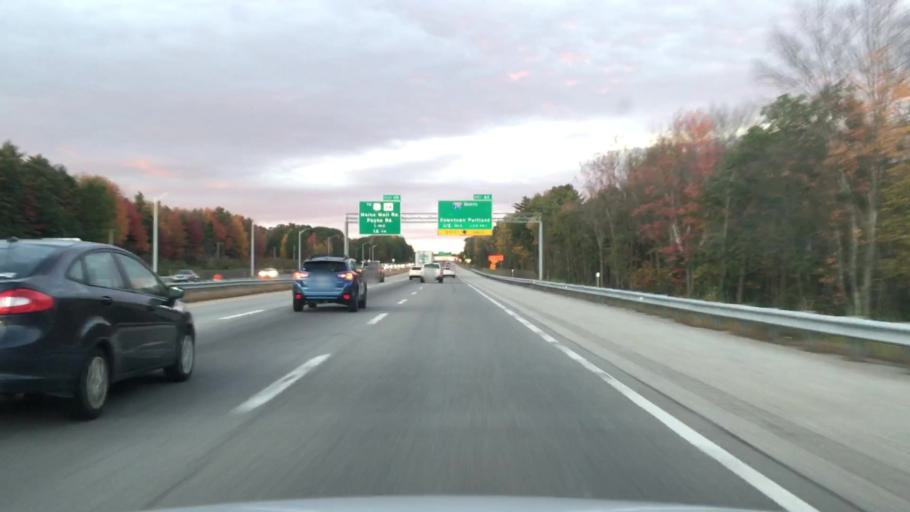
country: US
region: Maine
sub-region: Cumberland County
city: South Portland Gardens
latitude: 43.6161
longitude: -70.3608
